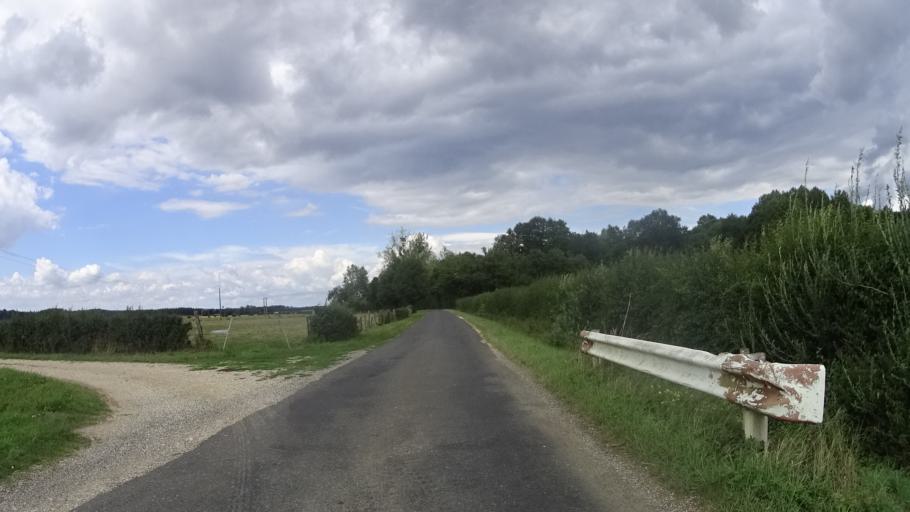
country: FR
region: Champagne-Ardenne
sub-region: Departement de la Haute-Marne
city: Villiers-en-Lieu
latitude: 48.6663
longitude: 4.8184
